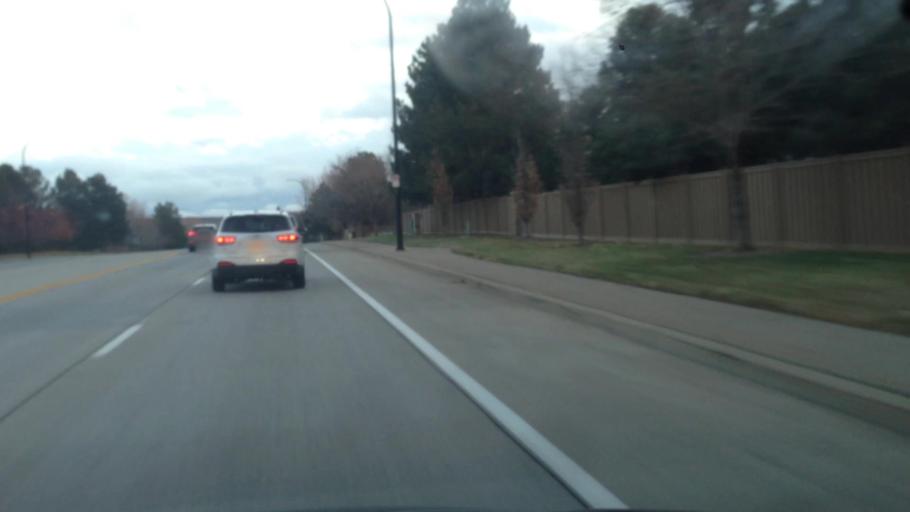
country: US
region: Colorado
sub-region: Douglas County
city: Carriage Club
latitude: 39.5389
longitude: -104.9096
